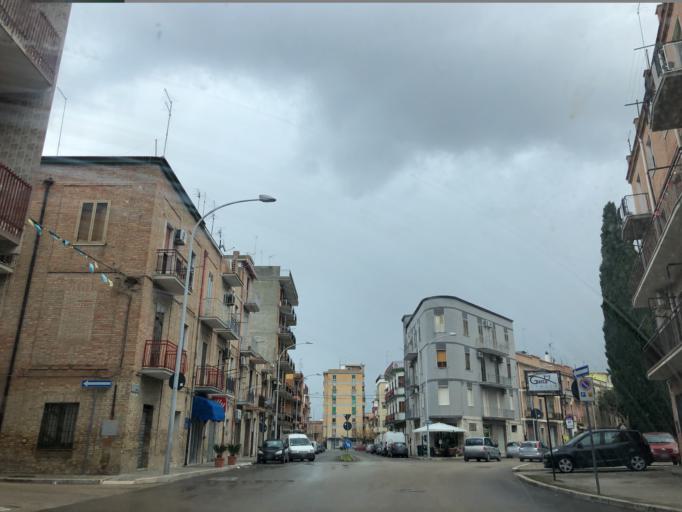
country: IT
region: Apulia
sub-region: Provincia di Foggia
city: Lucera
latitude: 41.5117
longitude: 15.3369
